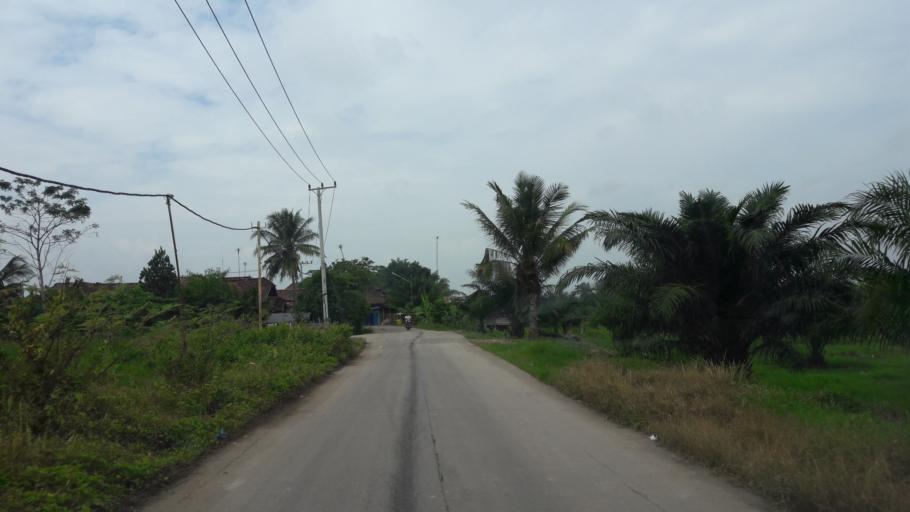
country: ID
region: South Sumatra
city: Gunungmenang
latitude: -3.2529
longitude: 104.1445
